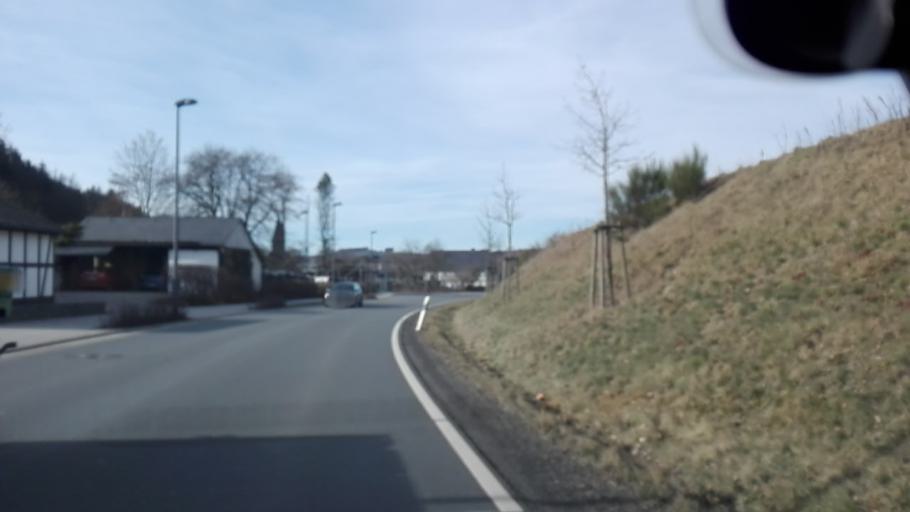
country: DE
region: North Rhine-Westphalia
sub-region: Regierungsbezirk Arnsberg
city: Bad Fredeburg
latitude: 51.1574
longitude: 8.3443
